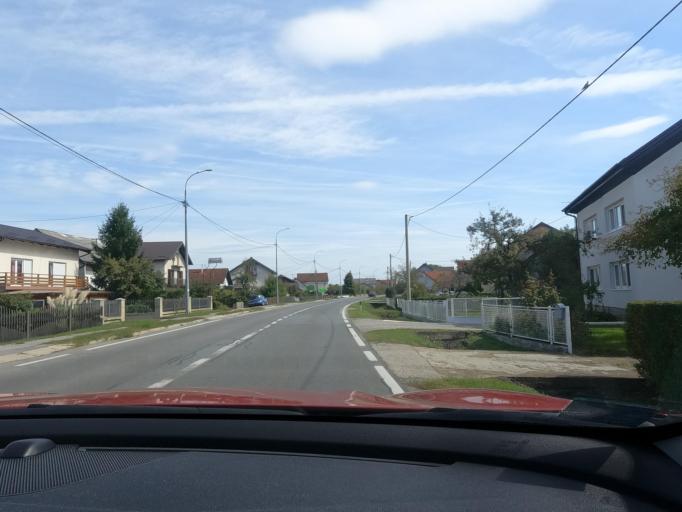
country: HR
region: Sisacko-Moslavacka
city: Budasevo
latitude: 45.4777
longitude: 16.4102
